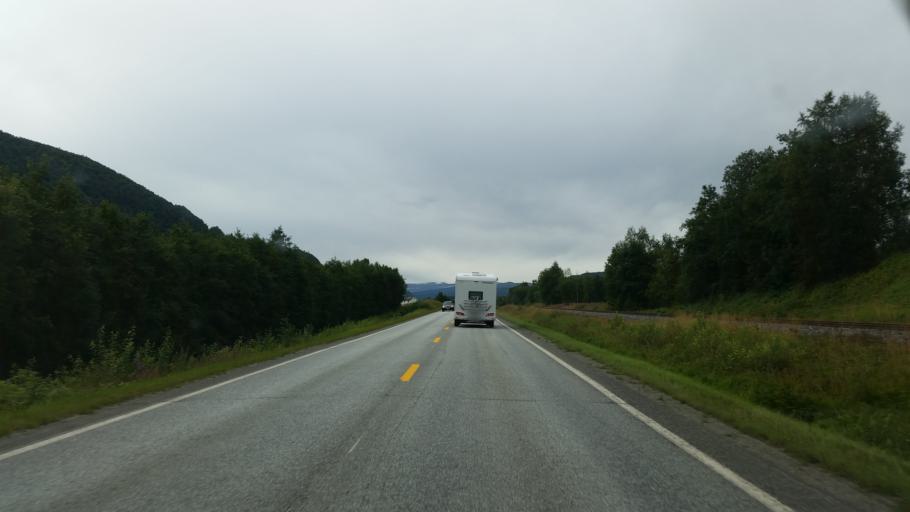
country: NO
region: Nordland
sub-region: Saltdal
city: Rognan
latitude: 67.0354
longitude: 15.3709
